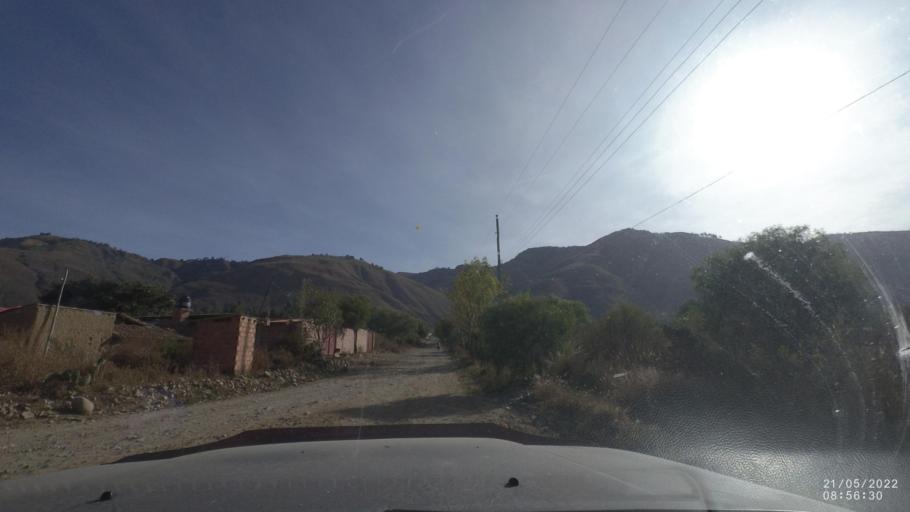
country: BO
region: Cochabamba
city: Cochabamba
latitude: -17.3811
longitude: -66.0412
